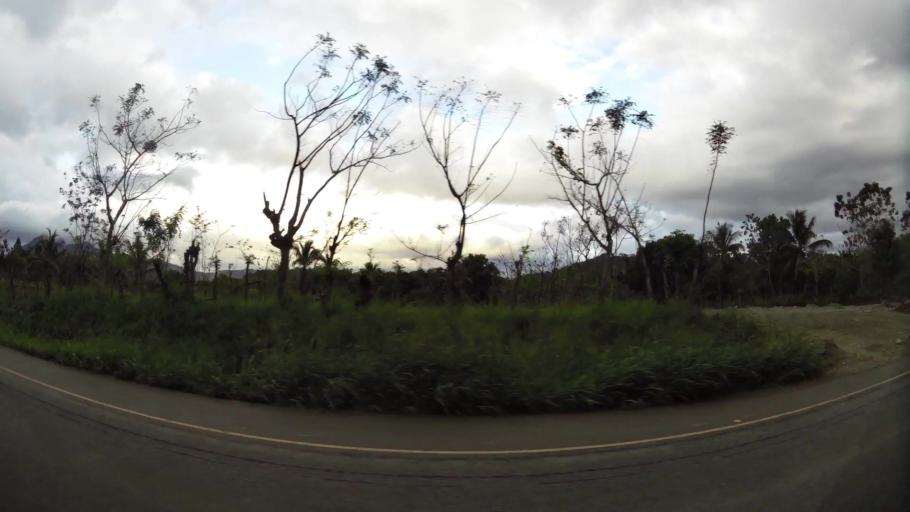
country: DO
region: San Cristobal
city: Villa Altagracia
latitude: 18.6347
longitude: -70.1679
